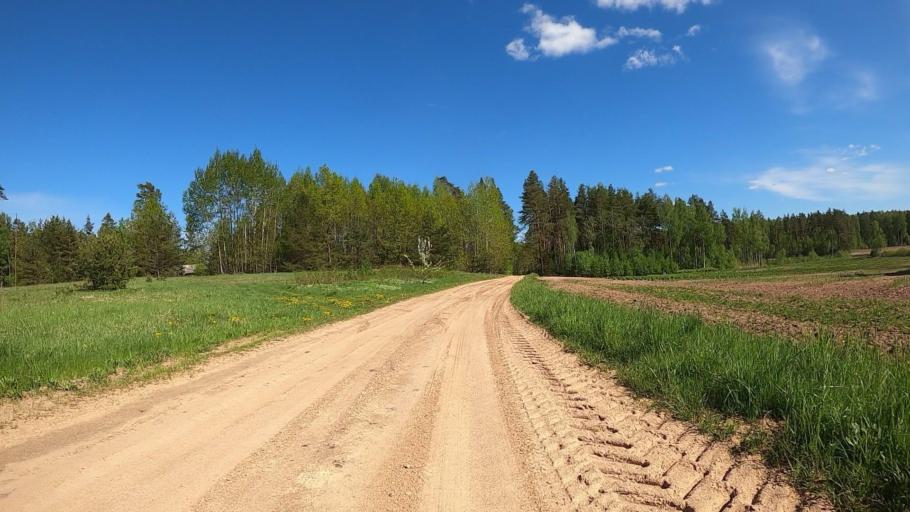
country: LV
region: Salaspils
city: Salaspils
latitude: 56.7910
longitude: 24.3172
